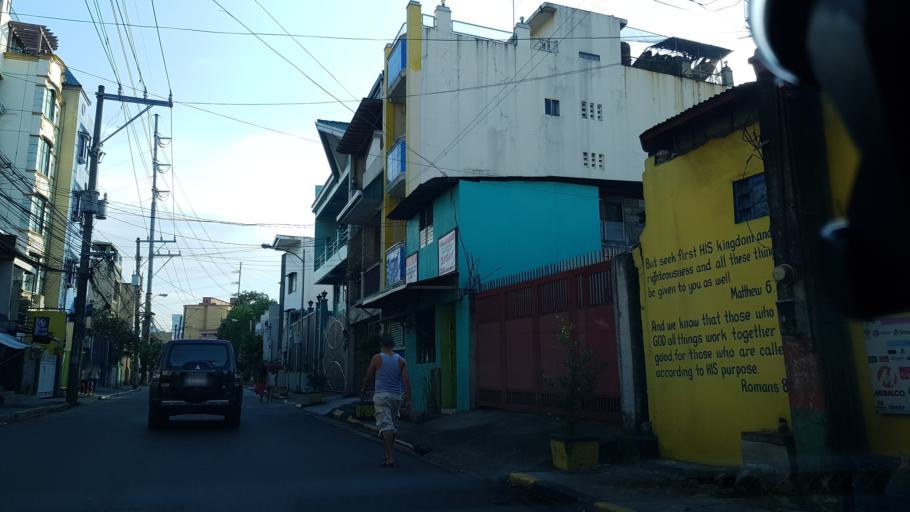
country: PH
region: Metro Manila
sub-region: Mandaluyong
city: Mandaluyong City
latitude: 14.5788
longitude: 121.0279
